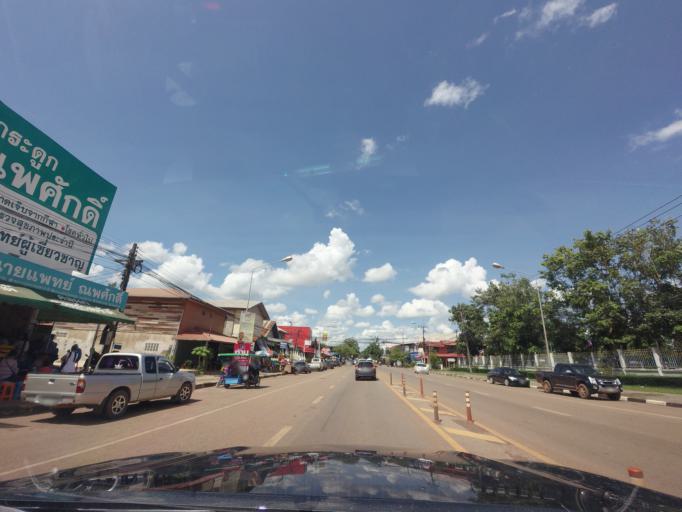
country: TH
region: Changwat Udon Thani
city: Ban Dung
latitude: 17.6925
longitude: 103.2578
